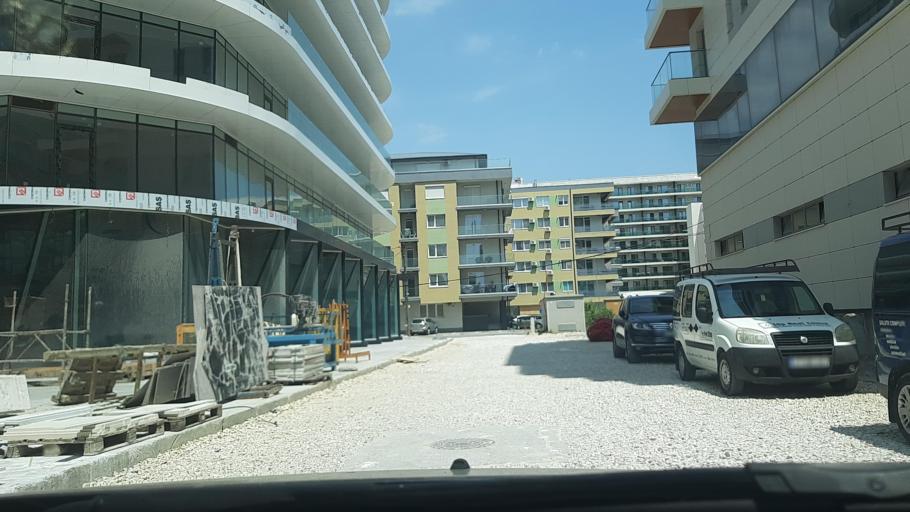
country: RO
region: Constanta
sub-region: Comuna Navodari
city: Navodari
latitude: 44.2874
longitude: 28.6218
